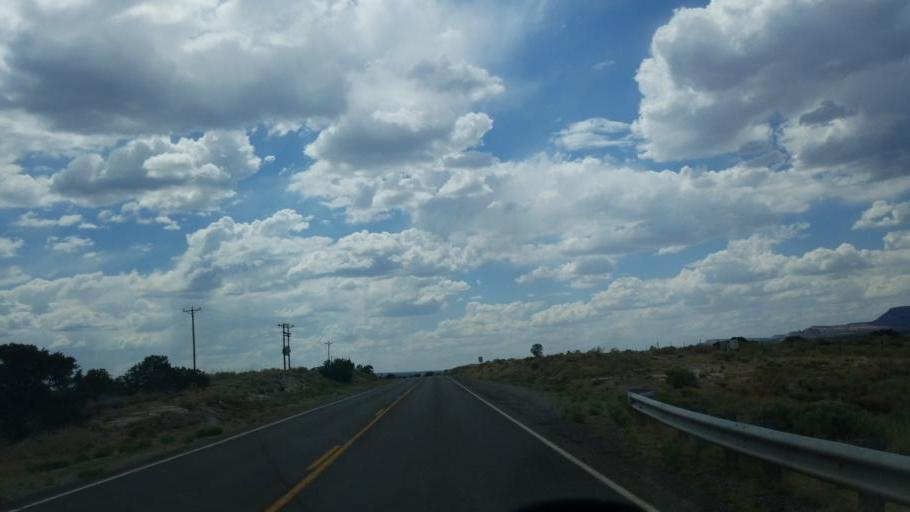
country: US
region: New Mexico
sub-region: McKinley County
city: Thoreau
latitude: 35.3887
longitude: -108.1612
